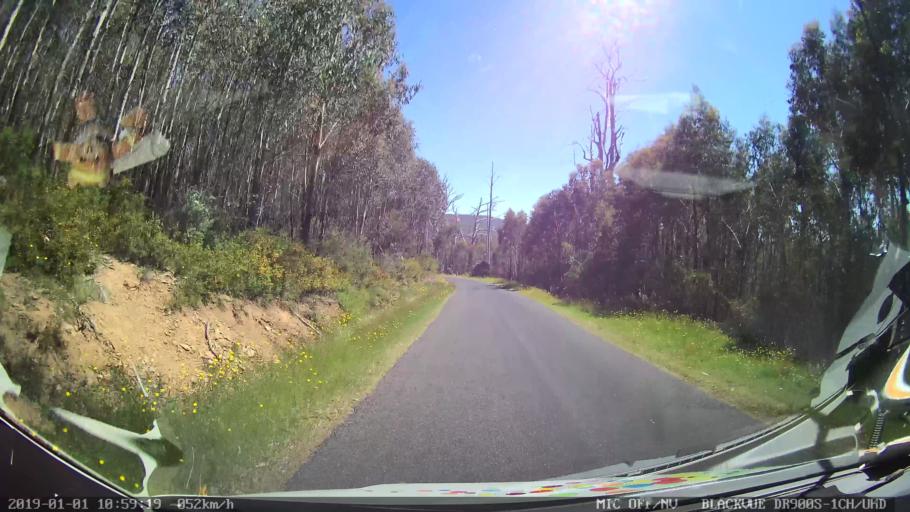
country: AU
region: New South Wales
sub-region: Snowy River
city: Jindabyne
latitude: -35.9860
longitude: 148.3986
